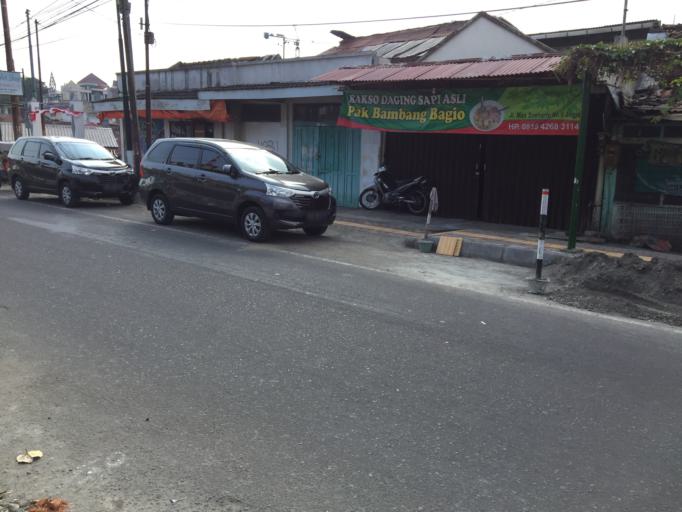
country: ID
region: Daerah Istimewa Yogyakarta
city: Yogyakarta
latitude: -7.7939
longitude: 110.3701
